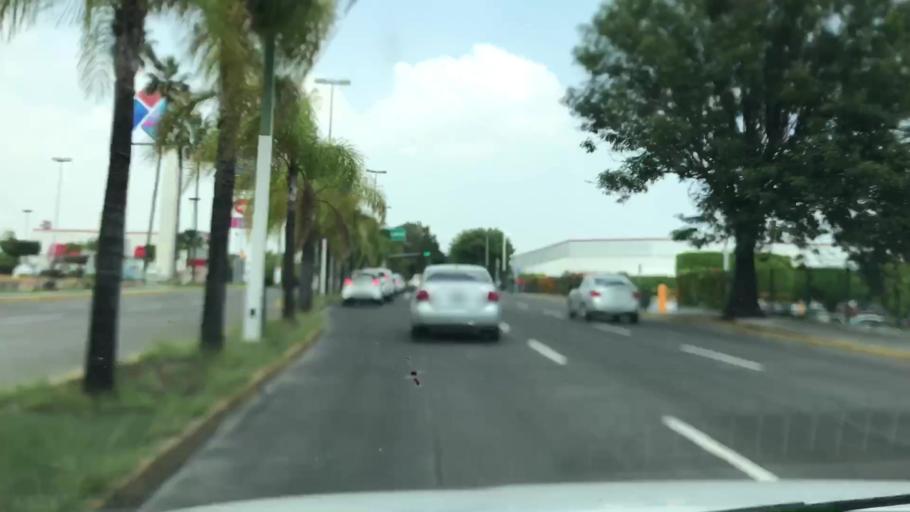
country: MX
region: Jalisco
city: Guadalajara
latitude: 20.6775
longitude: -103.4294
